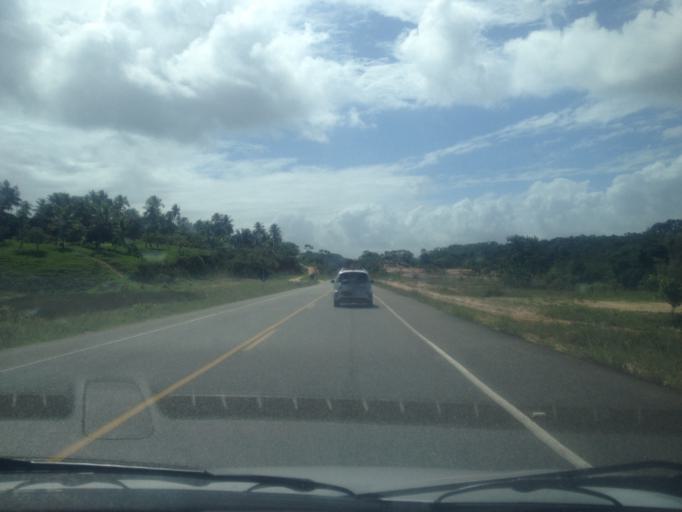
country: BR
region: Bahia
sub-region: Conde
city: Conde
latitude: -11.7119
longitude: -37.5732
